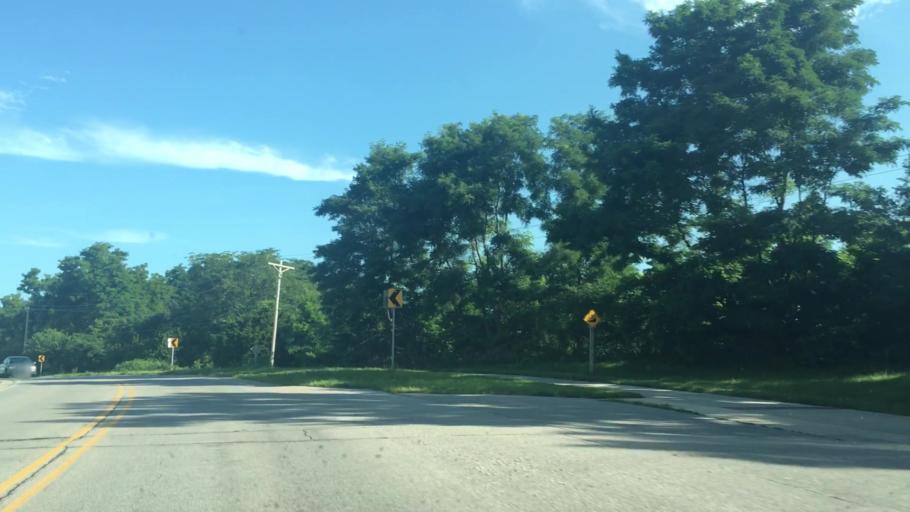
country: US
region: Iowa
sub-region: Johnson County
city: North Liberty
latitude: 41.7300
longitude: -91.5614
